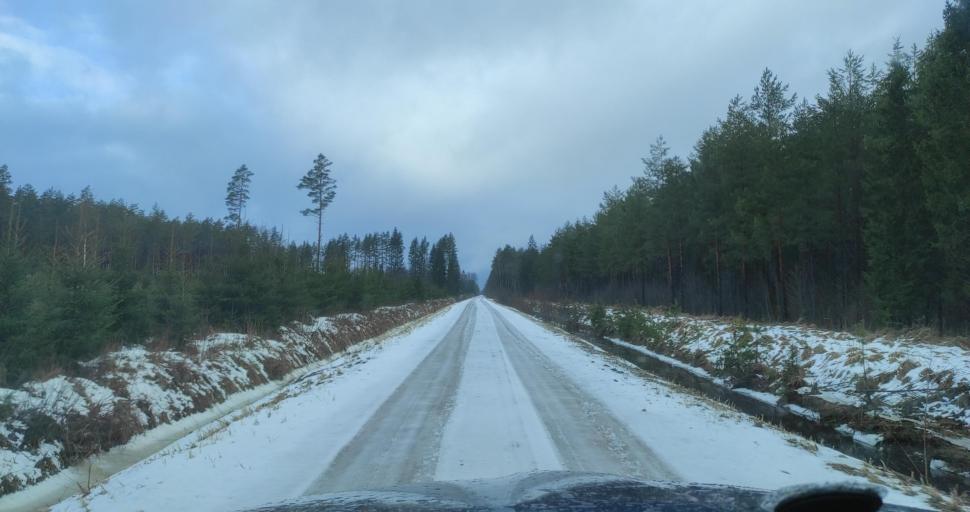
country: LV
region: Dundaga
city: Dundaga
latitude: 57.4007
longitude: 22.1071
